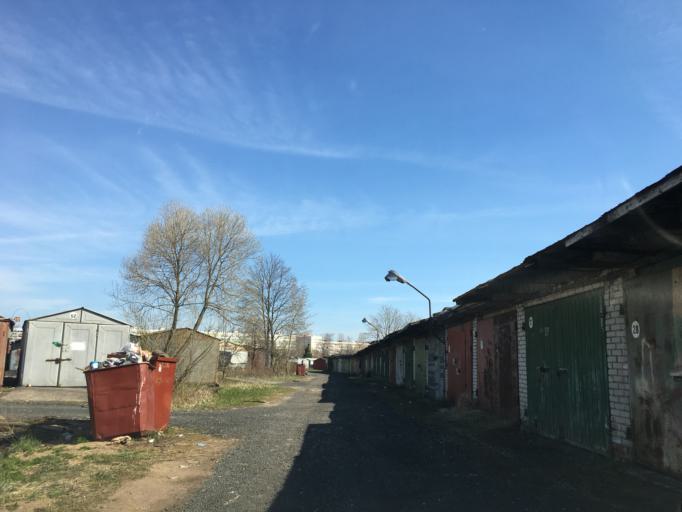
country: RU
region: St.-Petersburg
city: Uritsk
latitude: 59.8205
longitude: 30.1661
